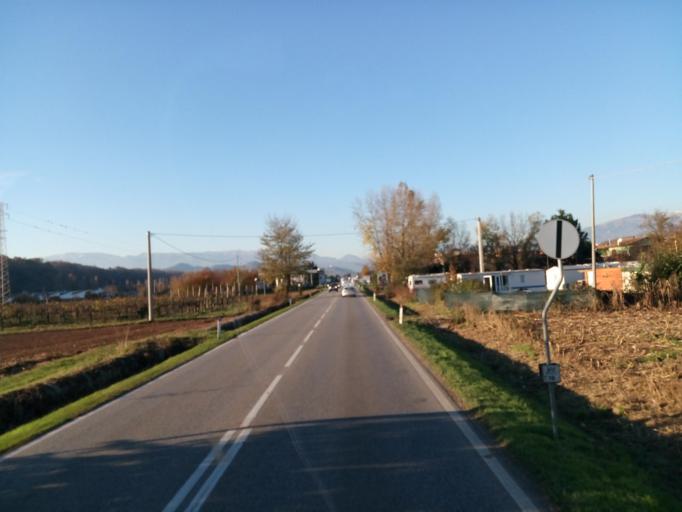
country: IT
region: Veneto
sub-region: Provincia di Treviso
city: Montebelluna
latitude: 45.7879
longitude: 12.0465
